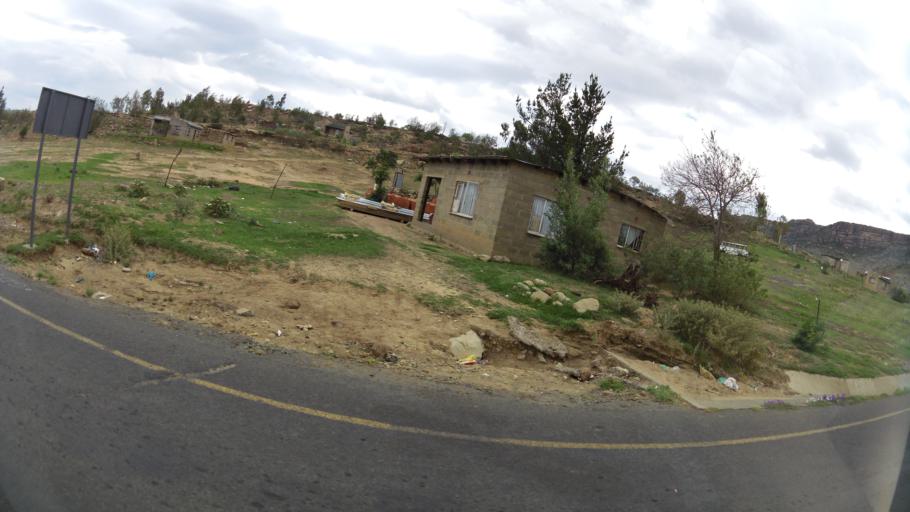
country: LS
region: Maseru
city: Maseru
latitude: -29.4033
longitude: 27.4721
